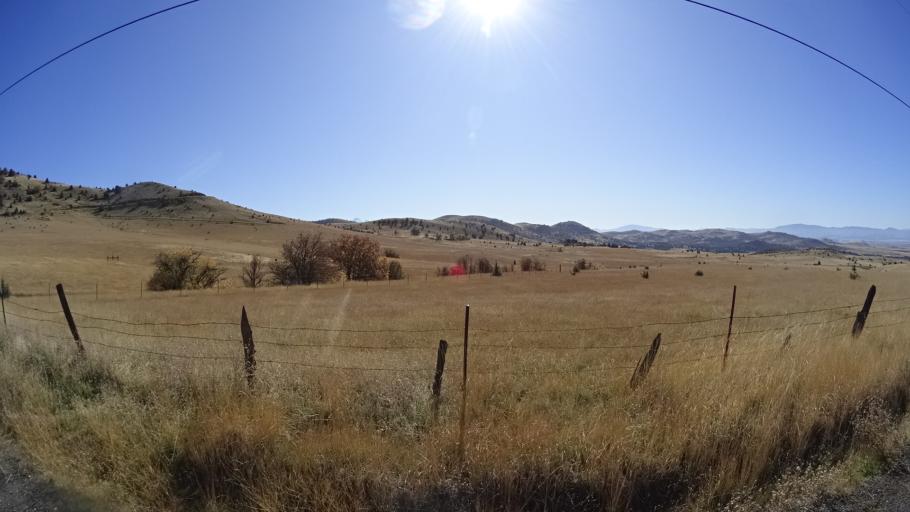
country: US
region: California
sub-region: Siskiyou County
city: Montague
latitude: 41.8304
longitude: -122.3496
